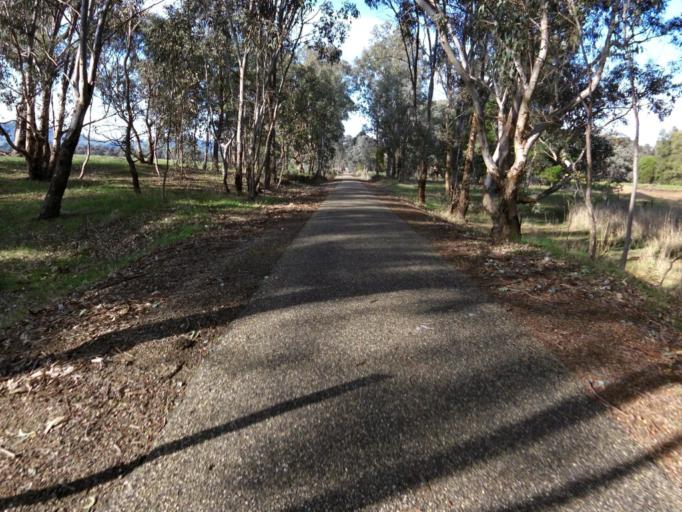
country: AU
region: Victoria
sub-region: Wangaratta
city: Wangaratta
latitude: -36.4146
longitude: 146.5499
